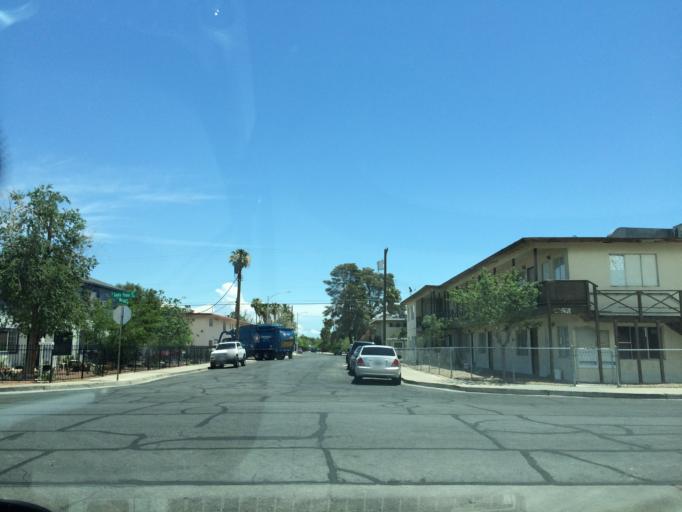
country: US
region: Nevada
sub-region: Clark County
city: Las Vegas
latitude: 36.1499
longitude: -115.1512
